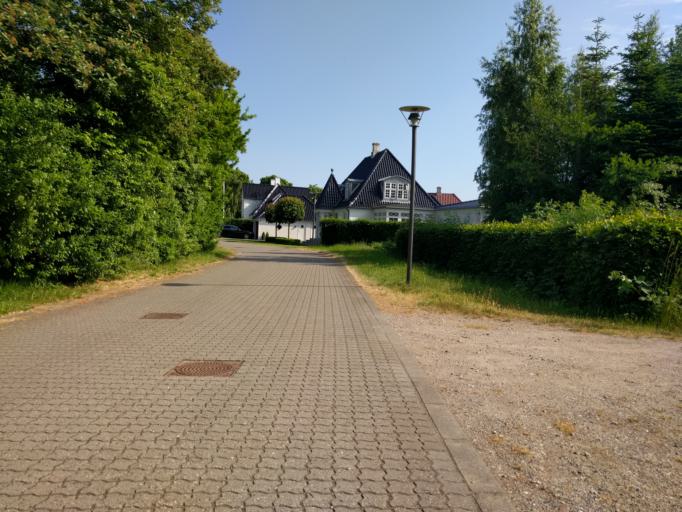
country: DK
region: South Denmark
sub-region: Kerteminde Kommune
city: Kerteminde
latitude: 55.4414
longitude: 10.6539
